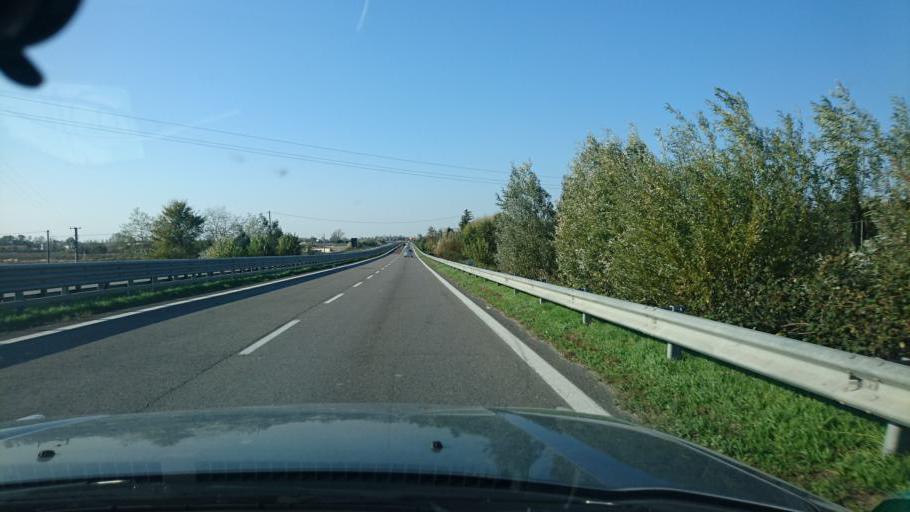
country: IT
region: Veneto
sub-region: Provincia di Padova
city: Monselice
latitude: 45.2089
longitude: 11.7536
